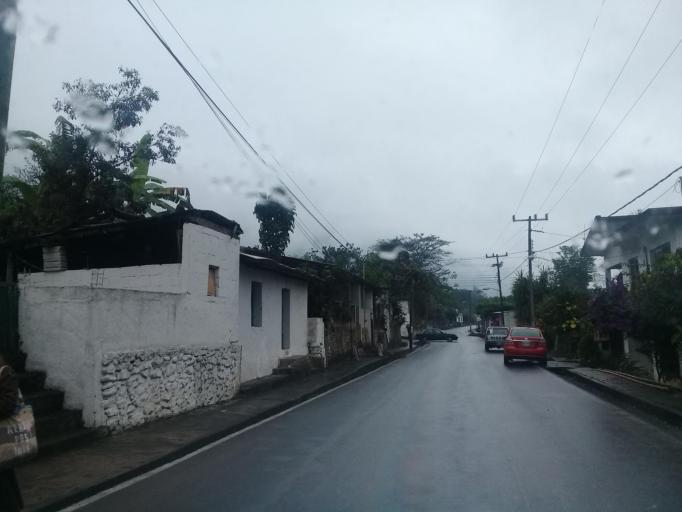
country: MX
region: Veracruz
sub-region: Amatlan de los Reyes
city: Centro de Readaptacion Social
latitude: 18.8076
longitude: -96.9582
